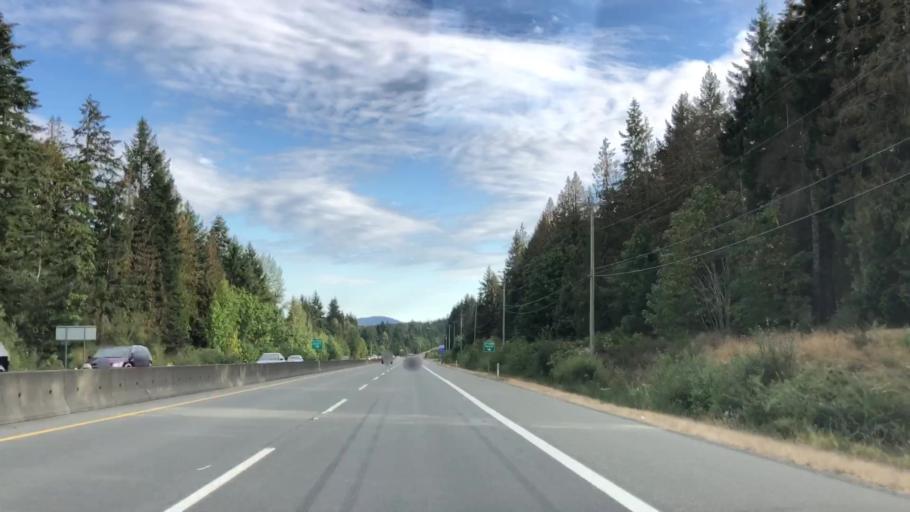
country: CA
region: British Columbia
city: North Saanich
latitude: 48.6179
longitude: -123.5435
